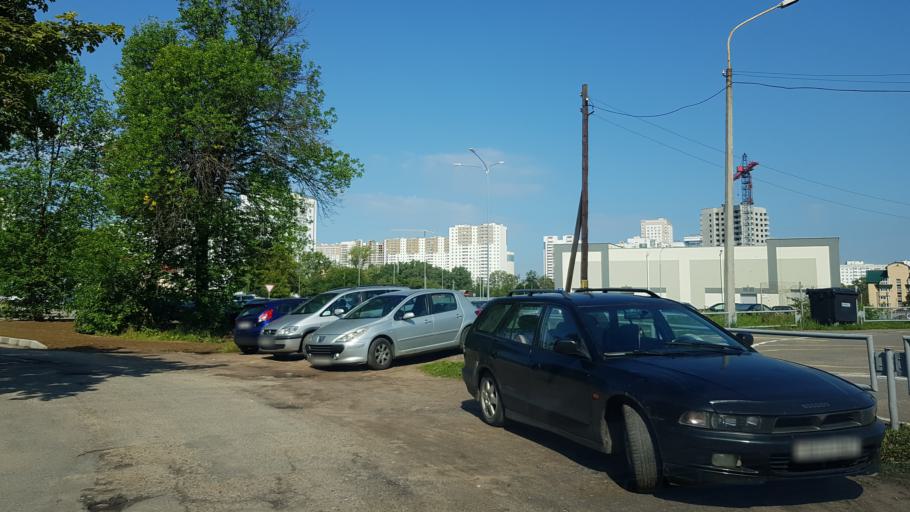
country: BY
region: Minsk
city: Minsk
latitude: 53.8837
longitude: 27.5274
